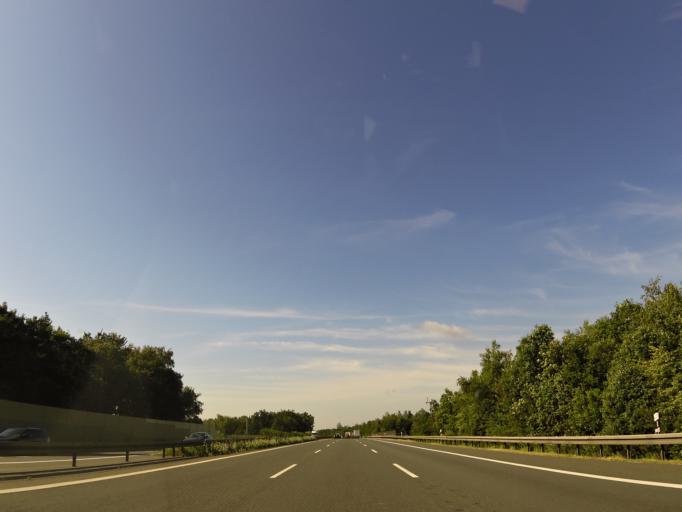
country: DE
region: Bavaria
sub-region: Regierungsbezirk Mittelfranken
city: Feucht
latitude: 49.3843
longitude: 11.2013
